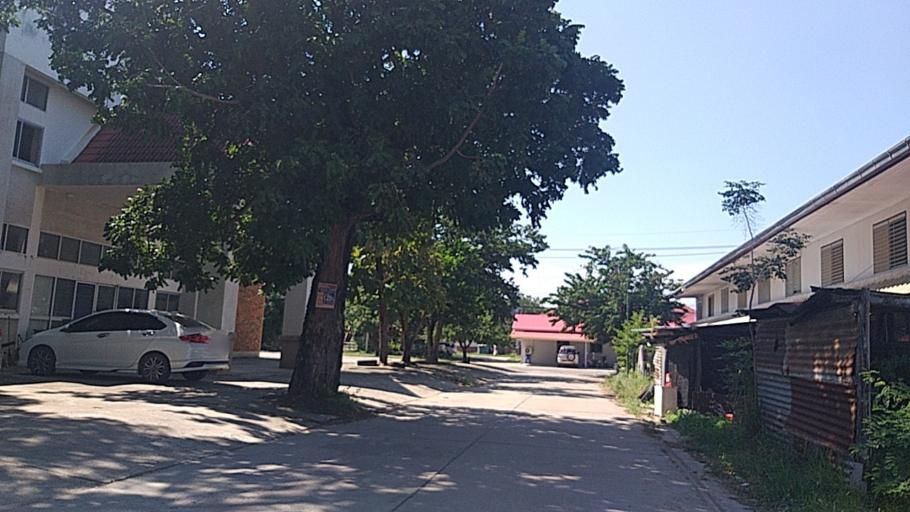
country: TH
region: Nakhon Ratchasima
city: Prathai
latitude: 15.5339
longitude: 102.7238
